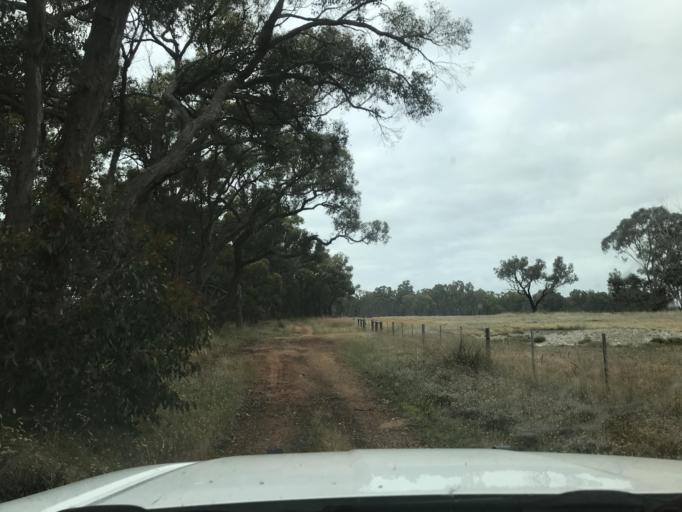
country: AU
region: South Australia
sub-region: Wattle Range
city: Penola
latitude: -37.1235
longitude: 141.1173
